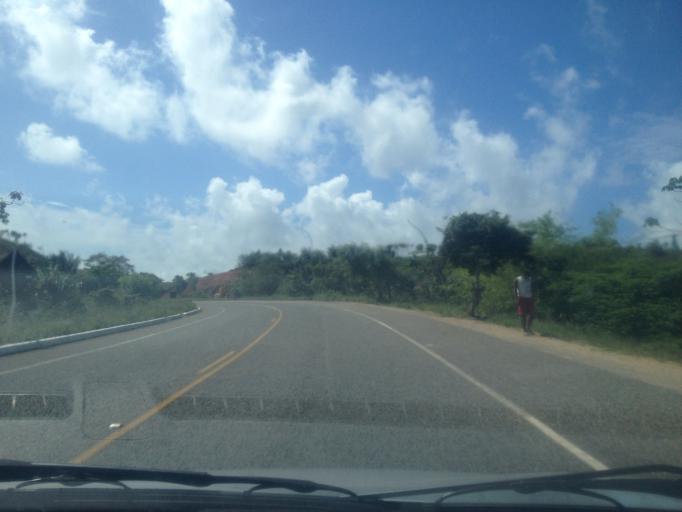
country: BR
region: Bahia
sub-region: Conde
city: Conde
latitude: -11.9071
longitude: -37.6540
